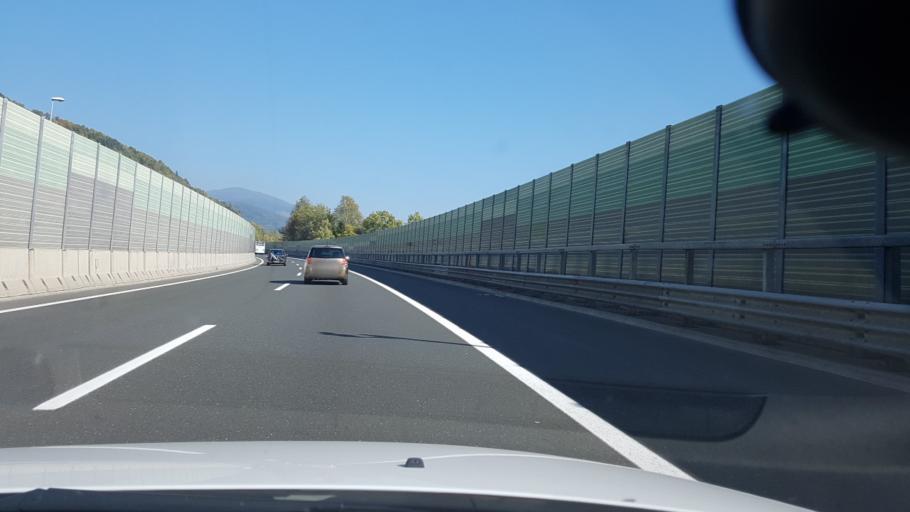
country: AT
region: Carinthia
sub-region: Politischer Bezirk Spittal an der Drau
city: Trebesing
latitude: 46.8880
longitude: 13.5176
